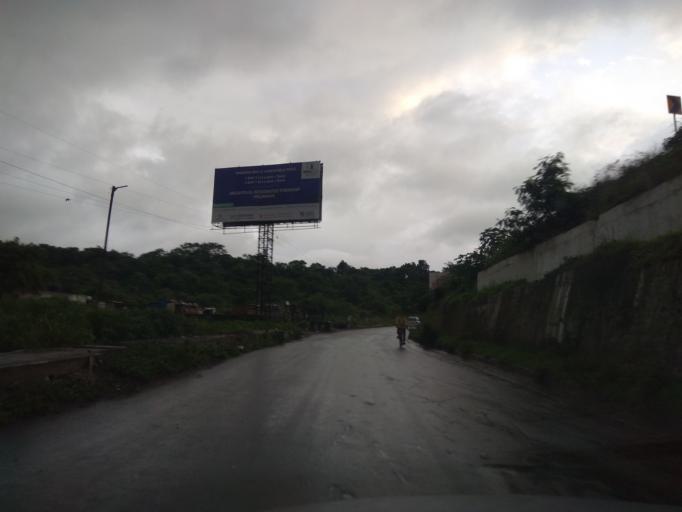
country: IN
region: Maharashtra
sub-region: Pune Division
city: Kharakvasla
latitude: 18.4942
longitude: 73.7877
